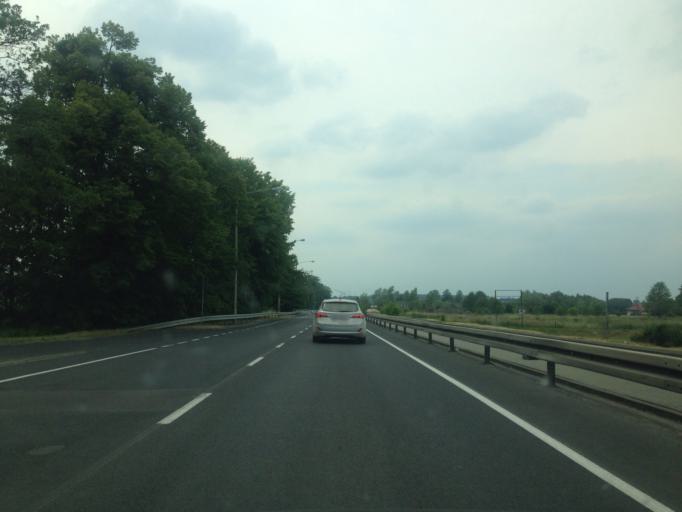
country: PL
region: Kujawsko-Pomorskie
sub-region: Grudziadz
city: Grudziadz
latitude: 53.5048
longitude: 18.8361
